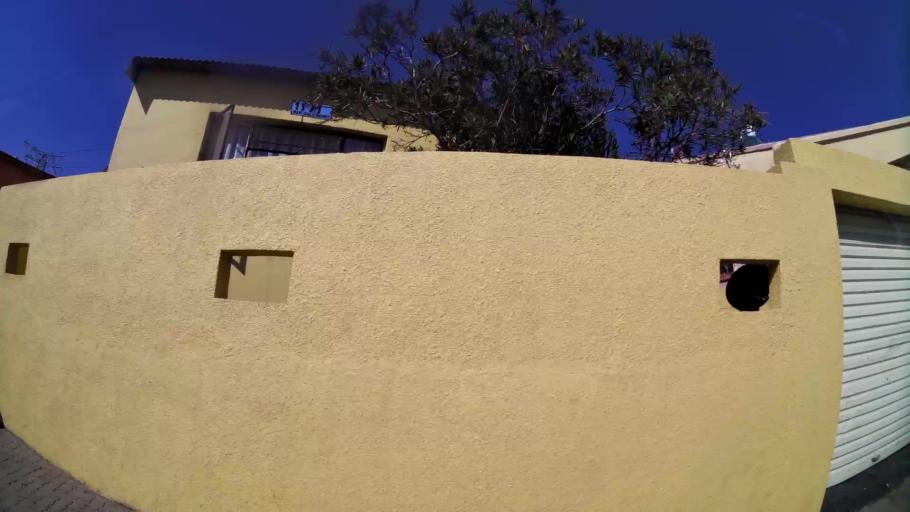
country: ZA
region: Gauteng
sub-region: City of Johannesburg Metropolitan Municipality
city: Johannesburg
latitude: -26.1860
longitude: 27.9766
